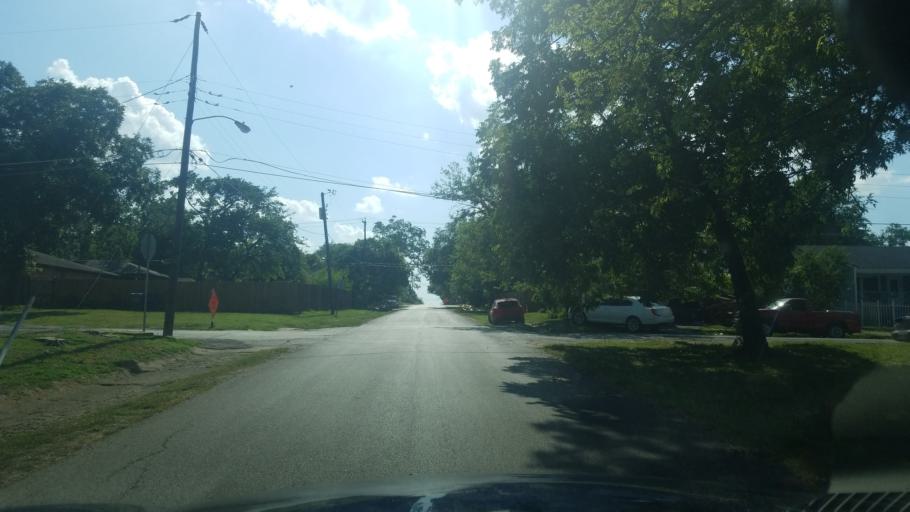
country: US
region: Texas
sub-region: Dallas County
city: Dallas
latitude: 32.7214
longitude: -96.8094
